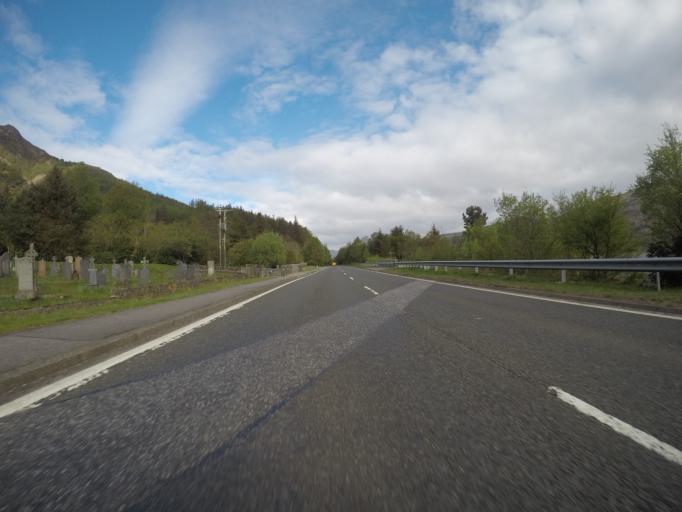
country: GB
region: Scotland
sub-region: Highland
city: Fort William
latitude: 56.6784
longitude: -5.1557
